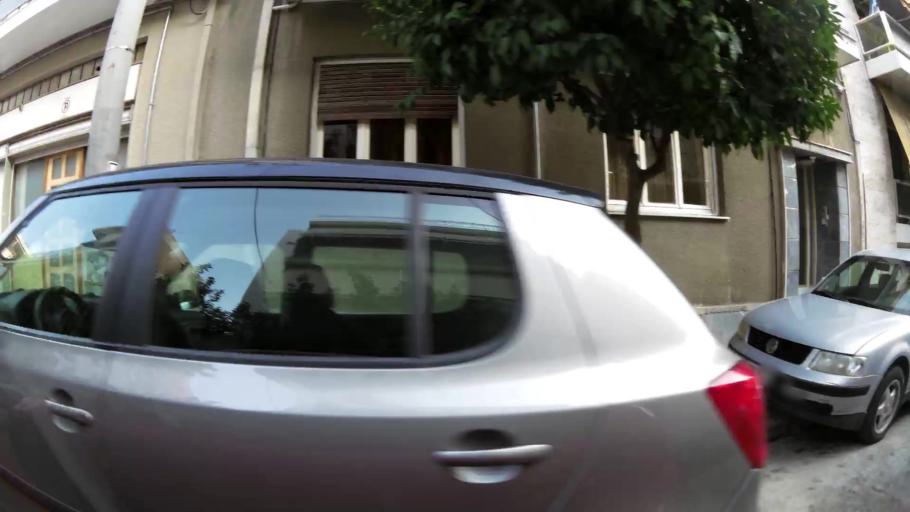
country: GR
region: Attica
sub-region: Nomarchia Athinas
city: Dhafni
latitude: 37.9497
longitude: 23.7286
